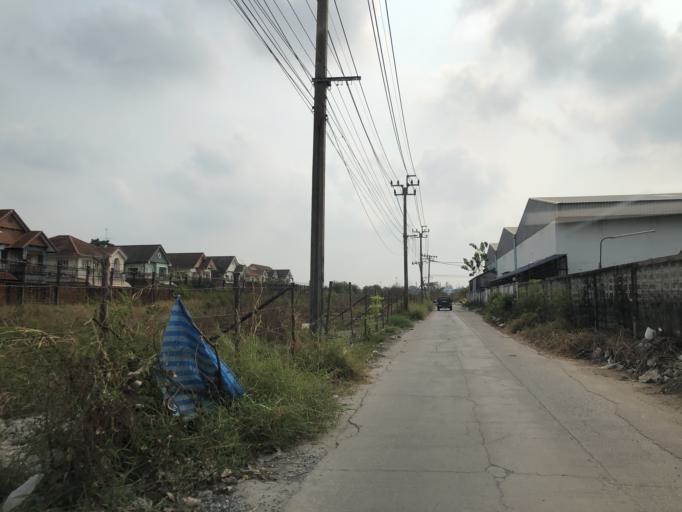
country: TH
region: Samut Prakan
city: Bang Bo District
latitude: 13.5839
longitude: 100.7118
